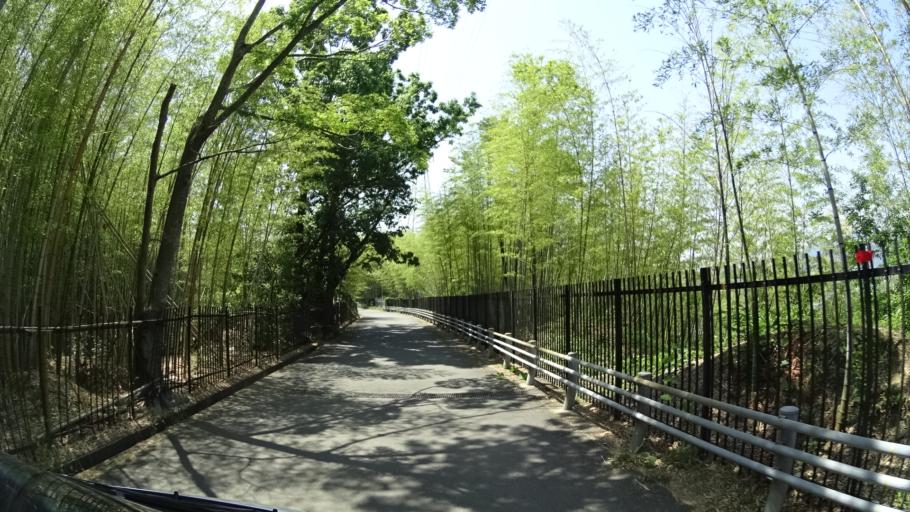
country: JP
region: Kyoto
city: Muko
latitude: 34.9623
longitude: 135.6851
